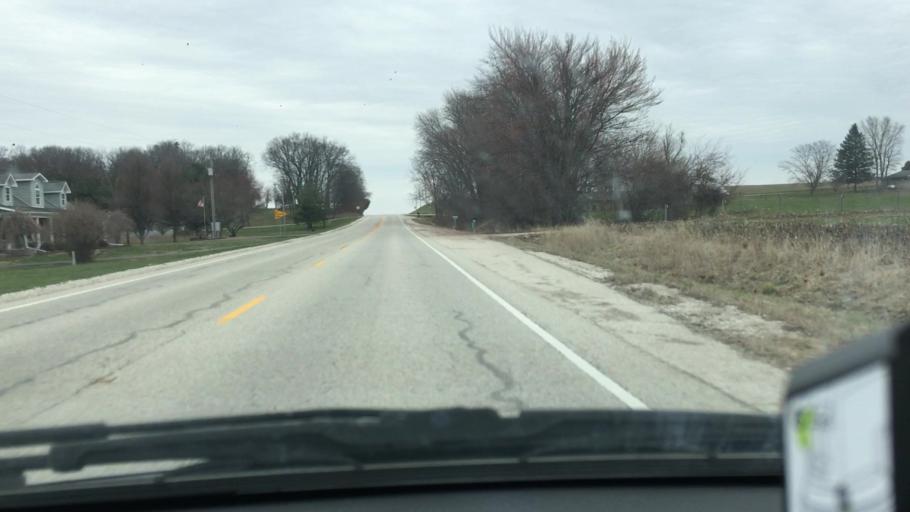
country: US
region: Indiana
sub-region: Greene County
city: Bloomfield
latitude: 38.9922
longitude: -87.0163
